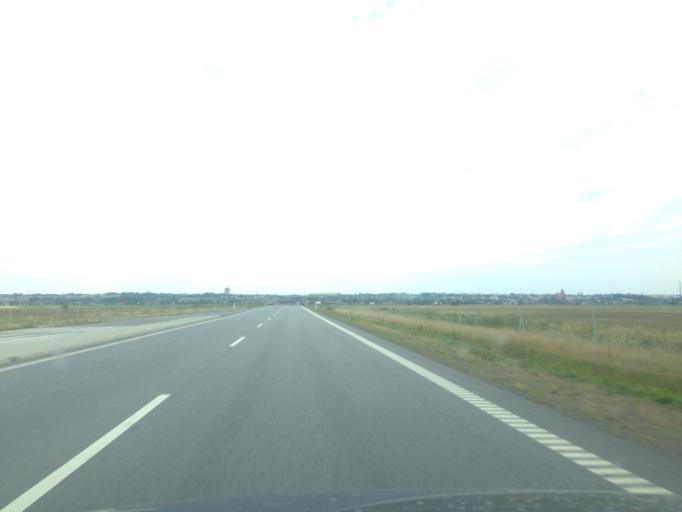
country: PL
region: Pomeranian Voivodeship
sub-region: Powiat kwidzynski
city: Kwidzyn
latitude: 53.7583
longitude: 18.8845
